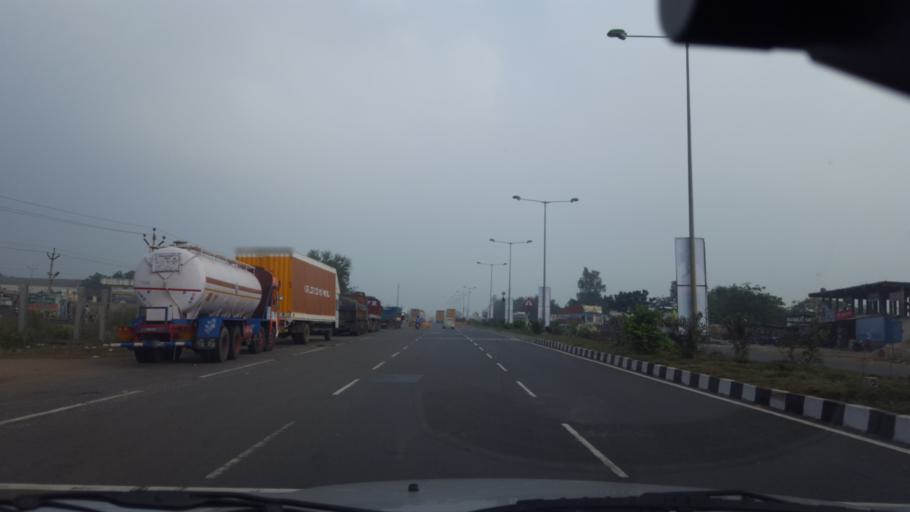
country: IN
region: Andhra Pradesh
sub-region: Prakasam
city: Addanki
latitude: 15.6844
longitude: 80.0179
